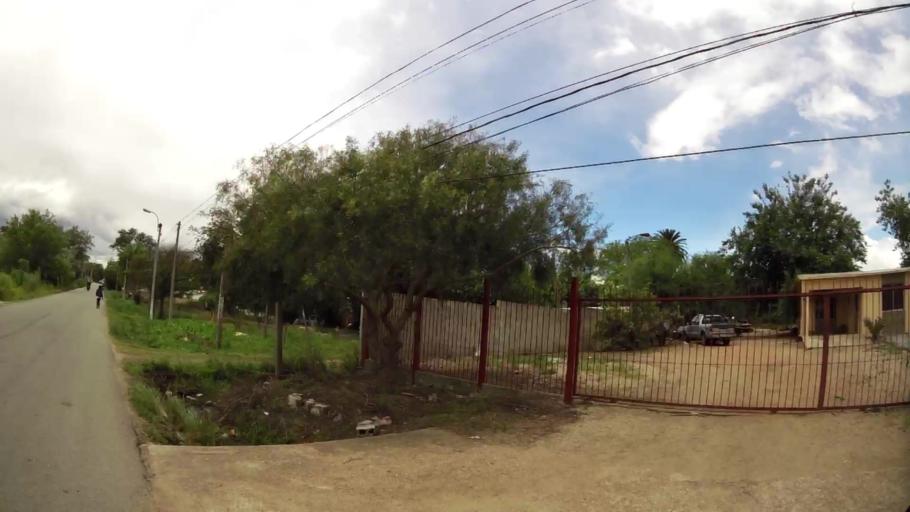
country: UY
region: Canelones
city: La Paz
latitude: -34.8031
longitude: -56.1608
